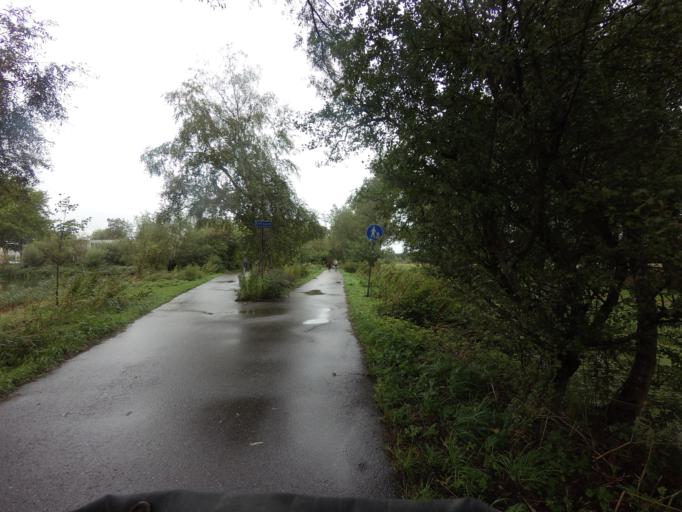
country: NL
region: Friesland
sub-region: Gemeente Leeuwarden
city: Bilgaard
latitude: 53.2180
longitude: 5.7954
